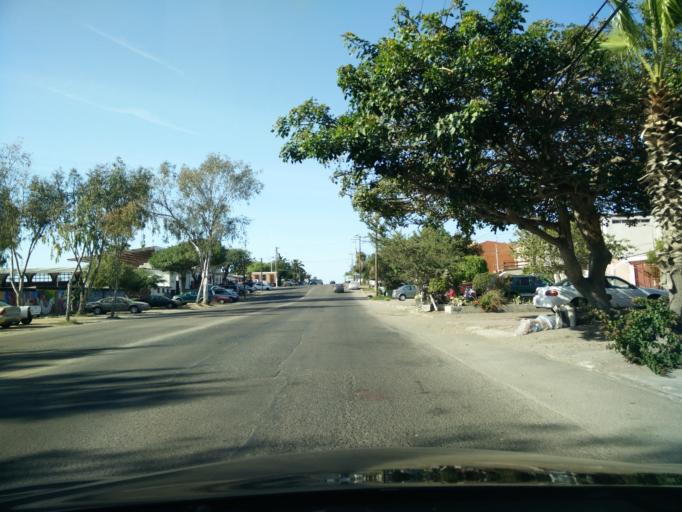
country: MX
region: Baja California
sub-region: Tijuana
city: La Esperanza [Granjas Familiares]
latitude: 32.5215
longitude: -117.1123
